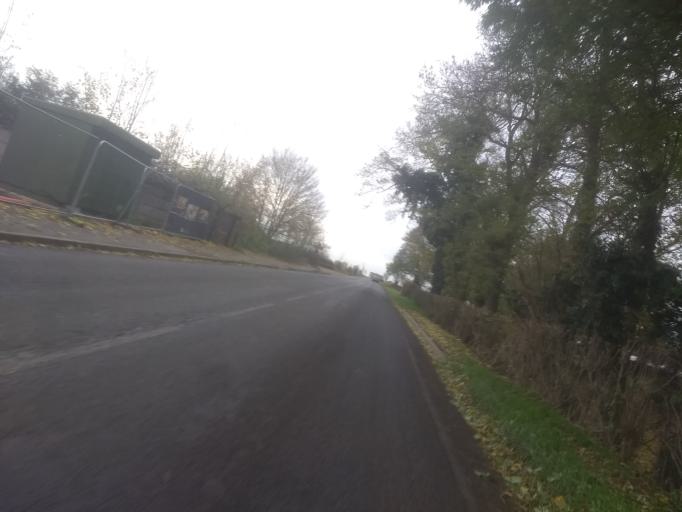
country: FR
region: Nord-Pas-de-Calais
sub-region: Departement du Pas-de-Calais
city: Dainville
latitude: 50.2793
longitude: 2.7370
